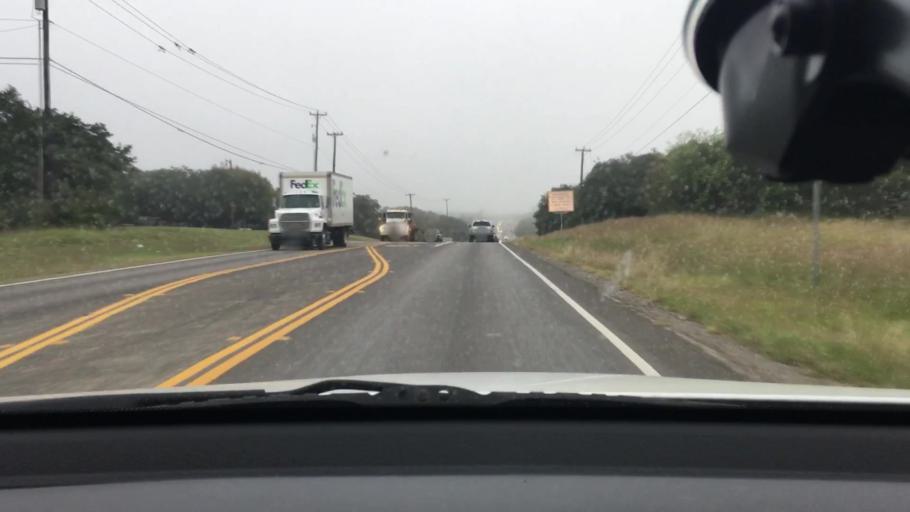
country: US
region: Texas
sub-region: Comal County
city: Garden Ridge
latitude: 29.6168
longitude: -98.3123
